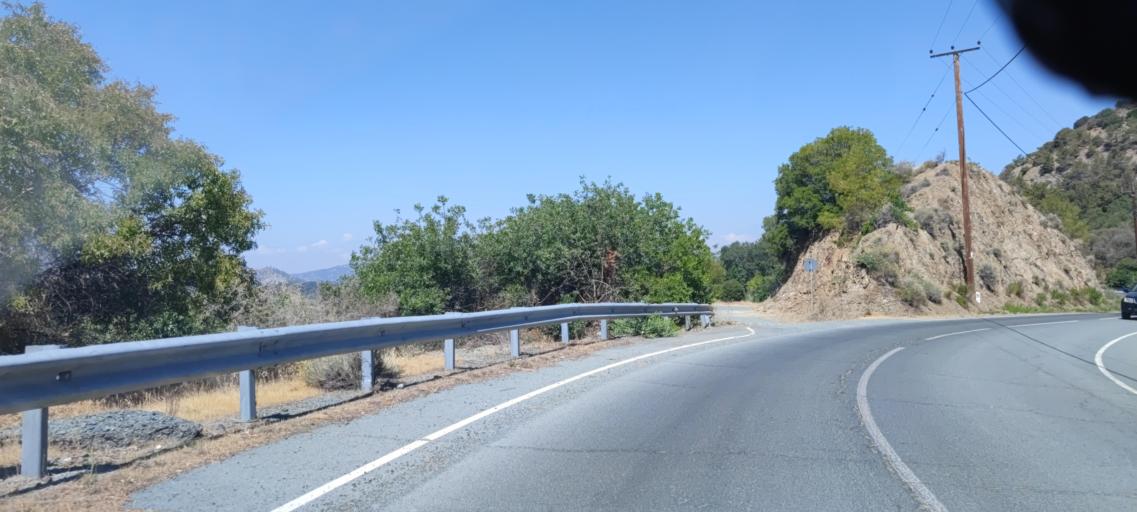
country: CY
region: Lefkosia
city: Kakopetria
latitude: 34.8963
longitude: 32.8254
